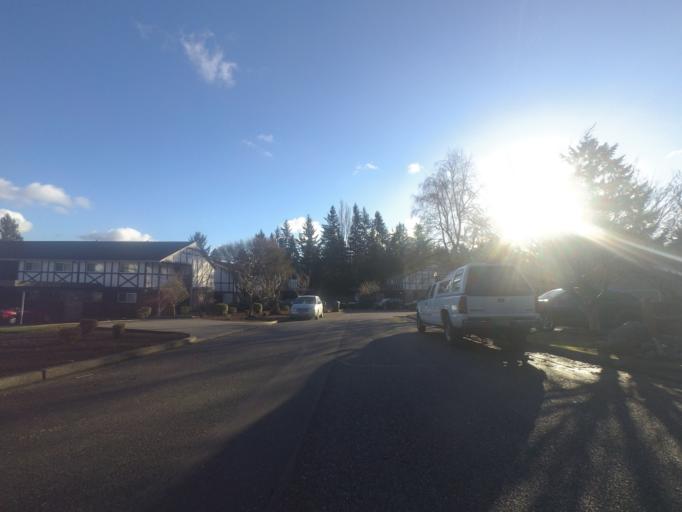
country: US
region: Washington
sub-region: Pierce County
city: Fircrest
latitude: 47.2219
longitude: -122.5193
